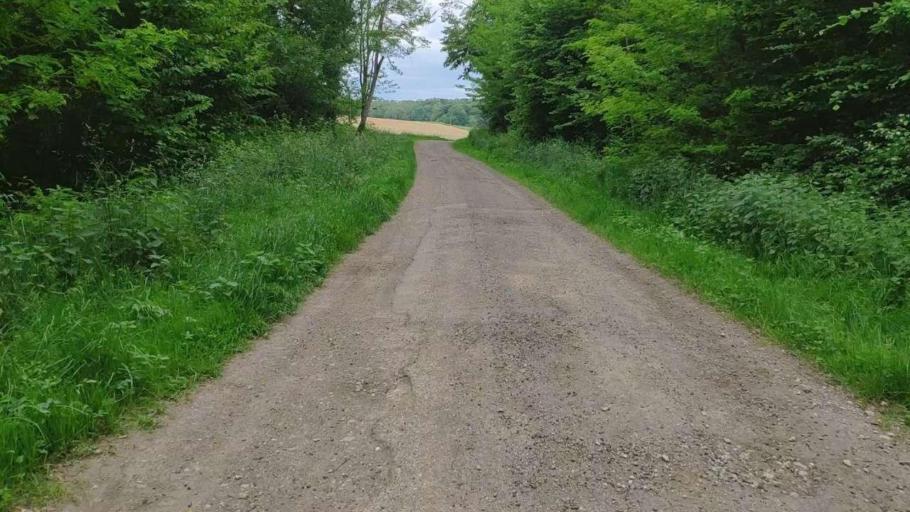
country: FR
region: Franche-Comte
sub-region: Departement du Jura
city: Bletterans
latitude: 46.7919
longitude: 5.5415
